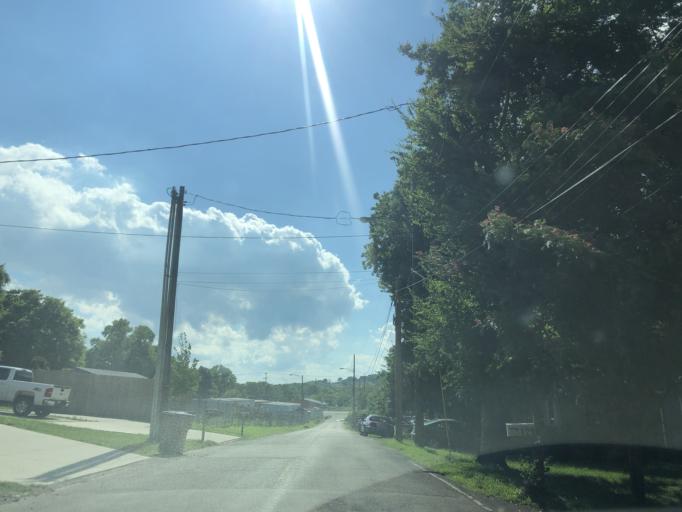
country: US
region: Tennessee
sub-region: Davidson County
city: Nashville
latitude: 36.2091
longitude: -86.7639
